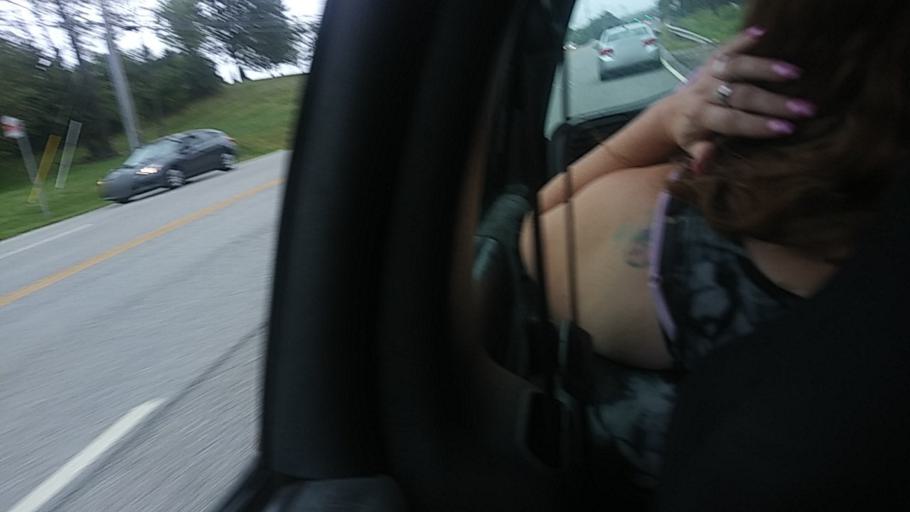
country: US
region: Ohio
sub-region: Summit County
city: Fairlawn
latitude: 41.1407
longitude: -81.6156
